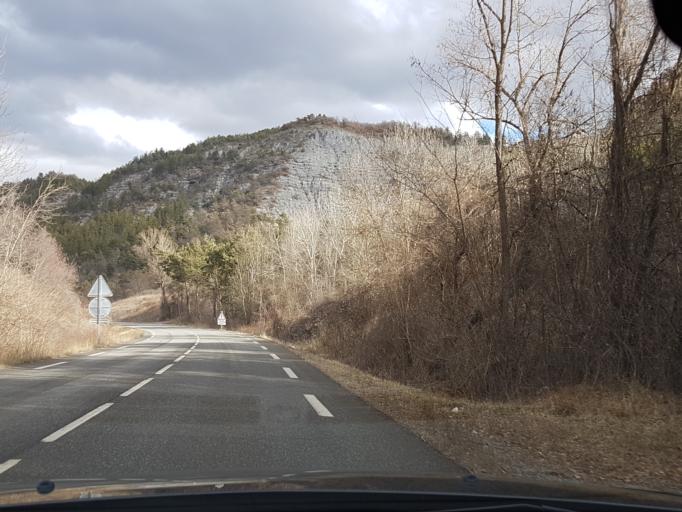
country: FR
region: Provence-Alpes-Cote d'Azur
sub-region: Departement des Hautes-Alpes
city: Tallard
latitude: 44.4930
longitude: 6.0810
